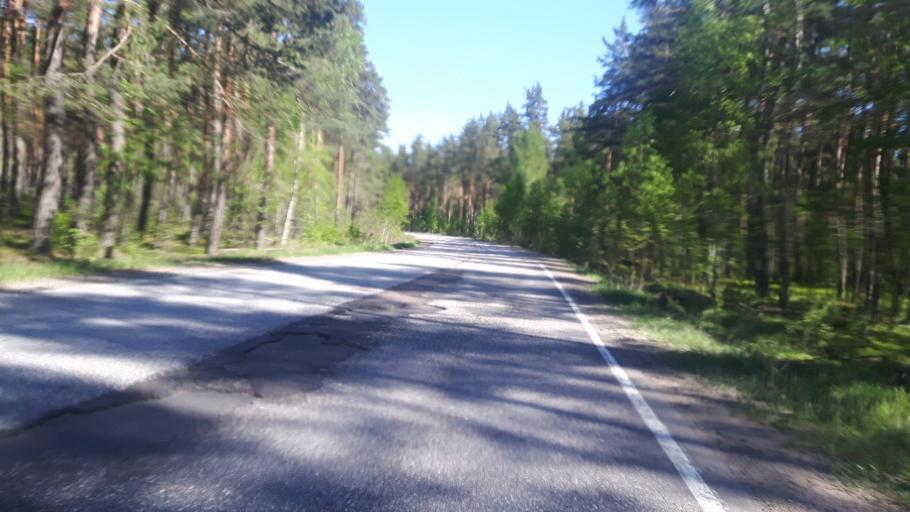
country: RU
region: Leningrad
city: Glebychevo
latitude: 60.2768
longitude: 28.9063
